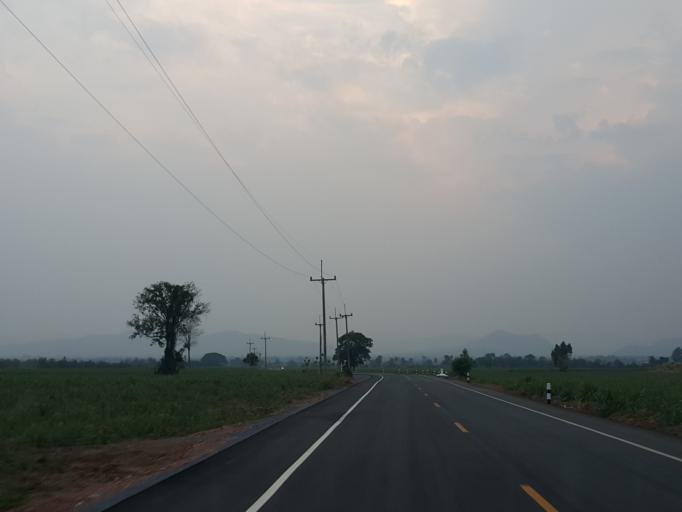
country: TH
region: Suphan Buri
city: Dan Chang
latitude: 14.9427
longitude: 99.6517
